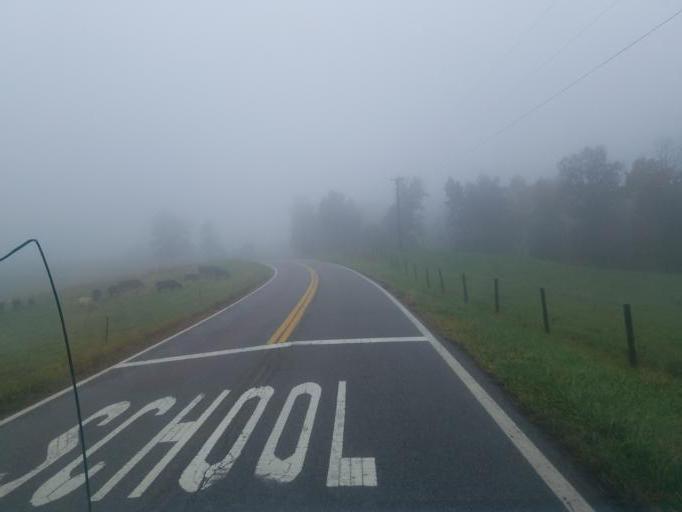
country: US
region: Ohio
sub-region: Morgan County
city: McConnelsville
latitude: 39.5463
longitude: -81.8110
